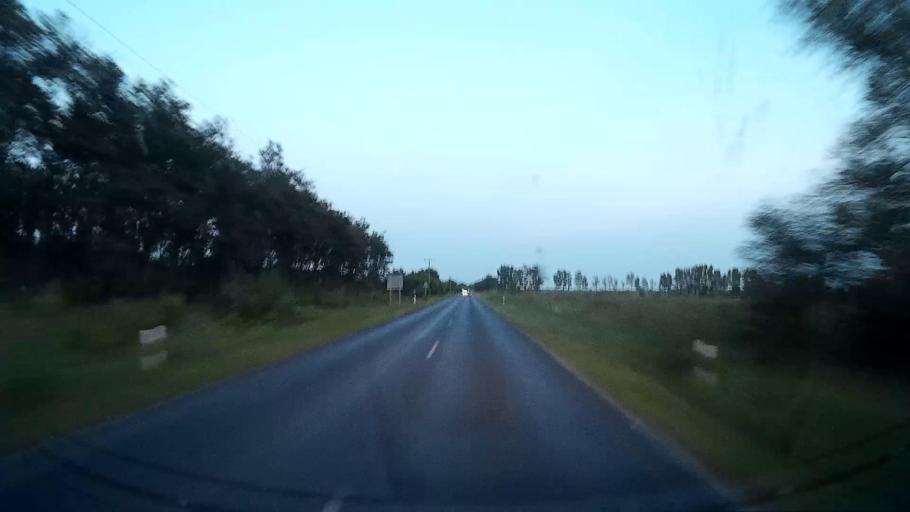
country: HU
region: Pest
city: Cegled
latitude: 47.1924
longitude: 19.7319
